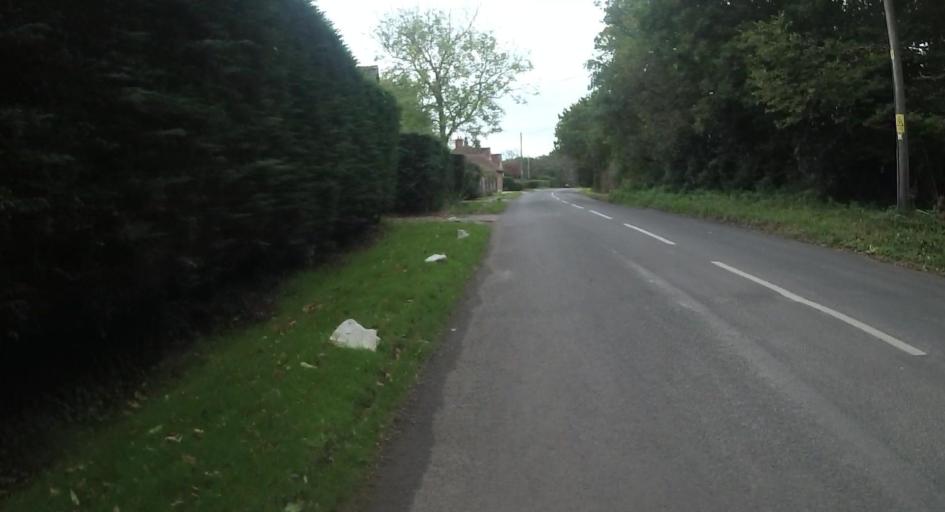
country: GB
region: England
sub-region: Hampshire
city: Odiham
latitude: 51.2844
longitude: -0.9016
